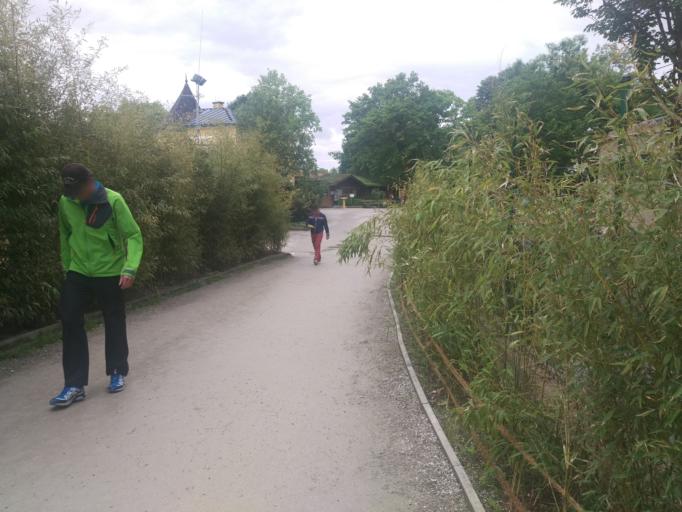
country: AT
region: Salzburg
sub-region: Politischer Bezirk Salzburg-Umgebung
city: Anif
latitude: 47.7567
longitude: 13.0648
